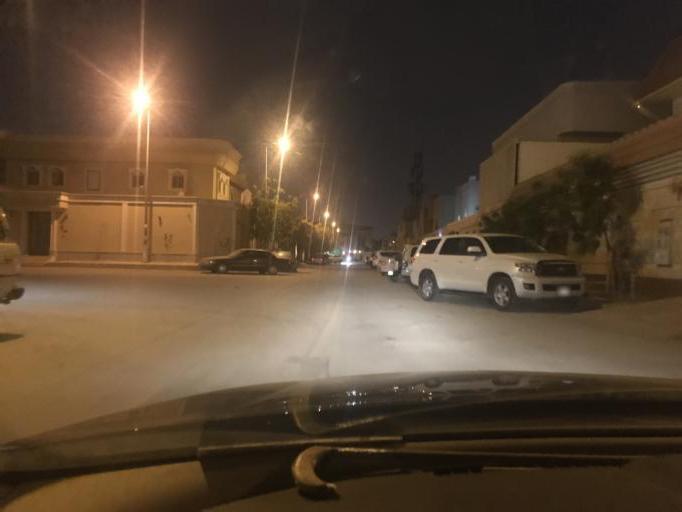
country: SA
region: Ar Riyad
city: Riyadh
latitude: 24.7501
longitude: 46.7770
